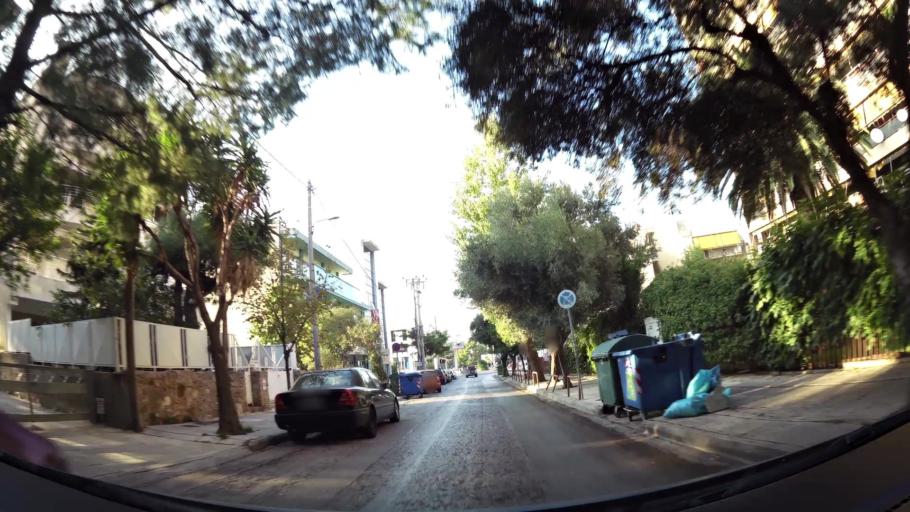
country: GR
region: Attica
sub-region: Nomarchia Athinas
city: Agia Paraskevi
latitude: 38.0118
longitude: 23.8164
